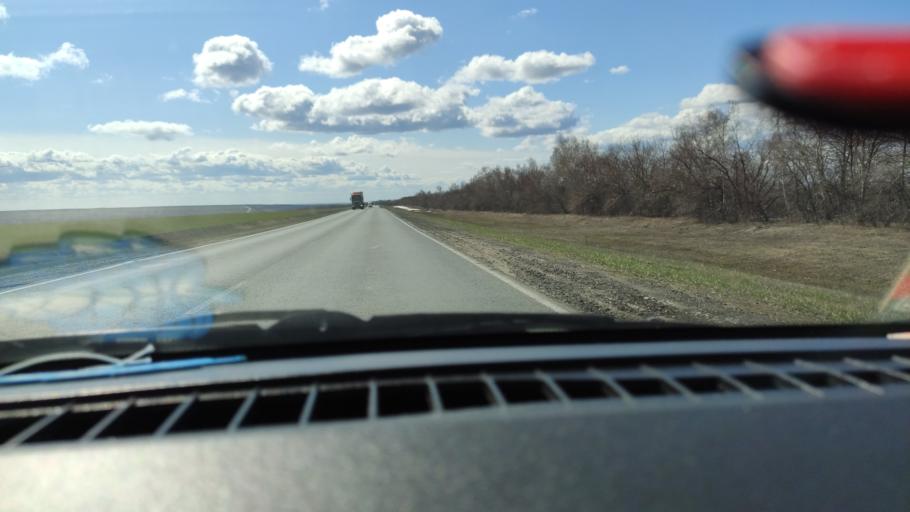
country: RU
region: Saratov
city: Dukhovnitskoye
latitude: 52.7683
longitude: 48.2369
